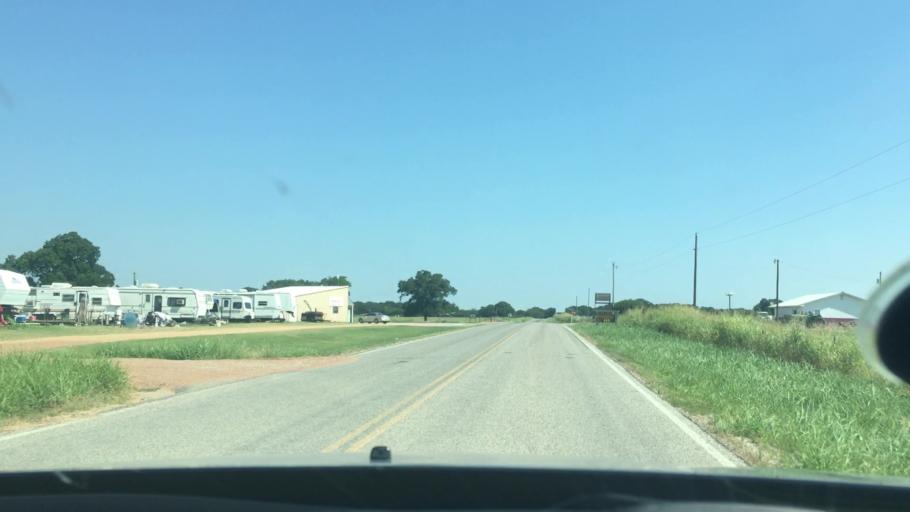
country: US
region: Oklahoma
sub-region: Johnston County
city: Tishomingo
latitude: 34.3089
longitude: -96.6184
